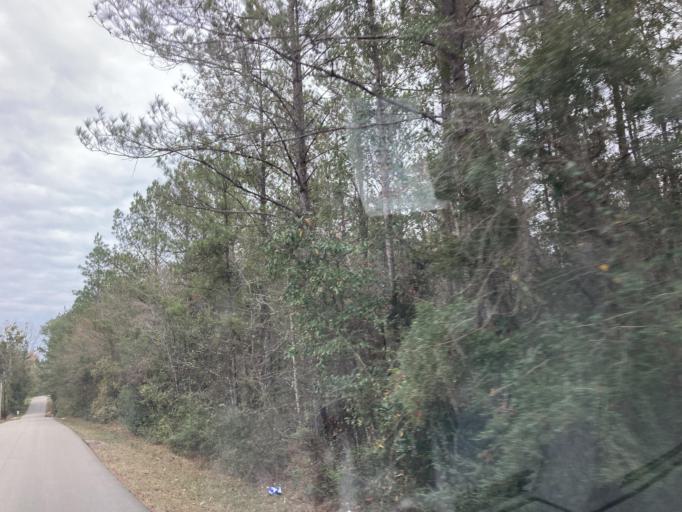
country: US
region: Mississippi
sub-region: Perry County
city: New Augusta
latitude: 31.0654
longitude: -89.2010
